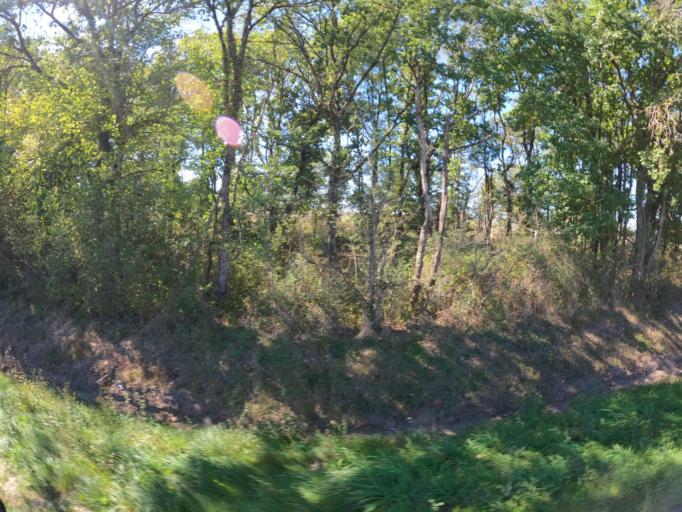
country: FR
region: Poitou-Charentes
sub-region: Departement de la Vienne
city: Lathus-Saint-Remy
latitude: 46.3688
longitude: 0.9359
